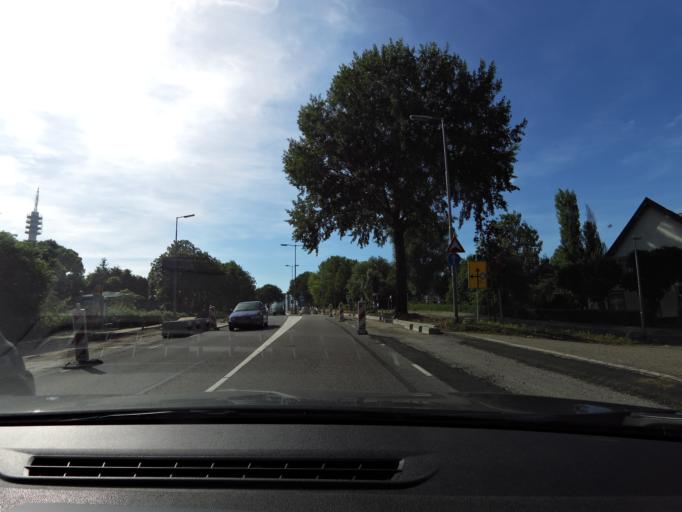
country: NL
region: South Holland
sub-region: Gemeente Rotterdam
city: Delfshaven
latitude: 51.8765
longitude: 4.4577
